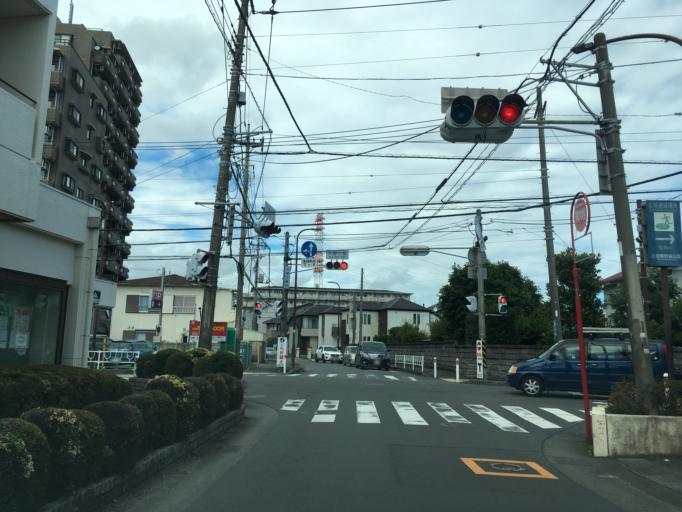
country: JP
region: Tokyo
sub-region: Machida-shi
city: Machida
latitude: 35.5529
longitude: 139.4218
